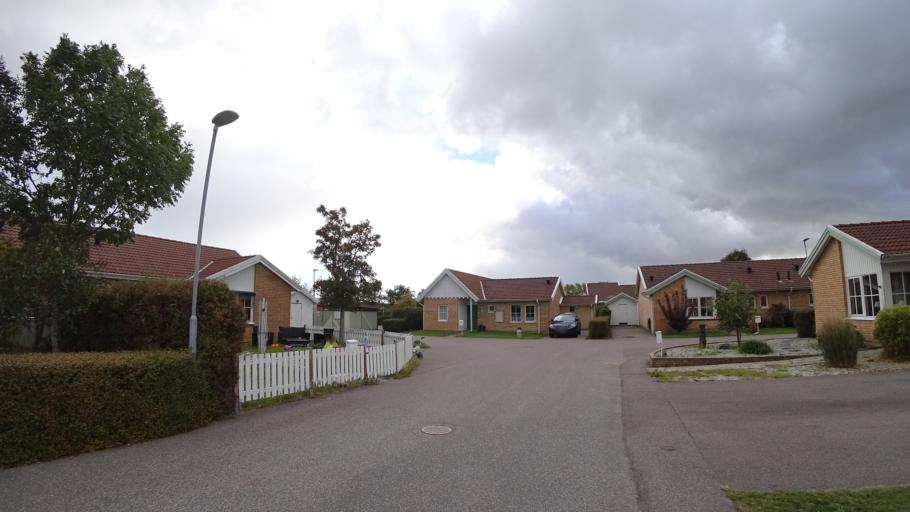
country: SE
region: Skane
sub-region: Kavlinge Kommun
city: Loddekopinge
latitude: 55.7622
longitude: 13.0225
